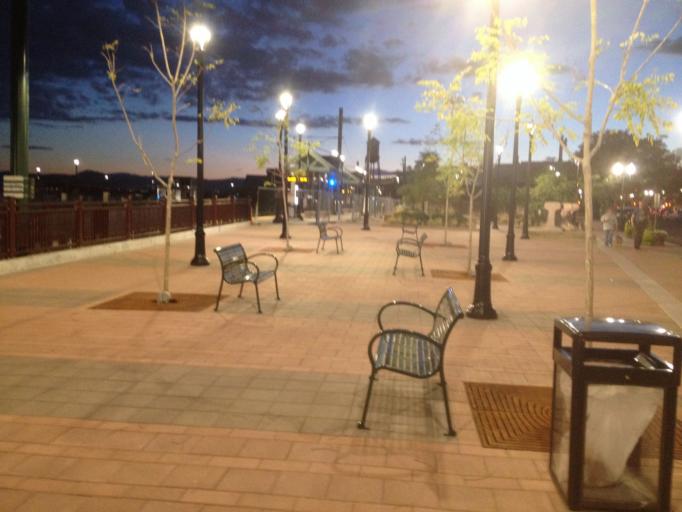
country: US
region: Colorado
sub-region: Jefferson County
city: Arvada
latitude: 39.7993
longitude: -105.0796
